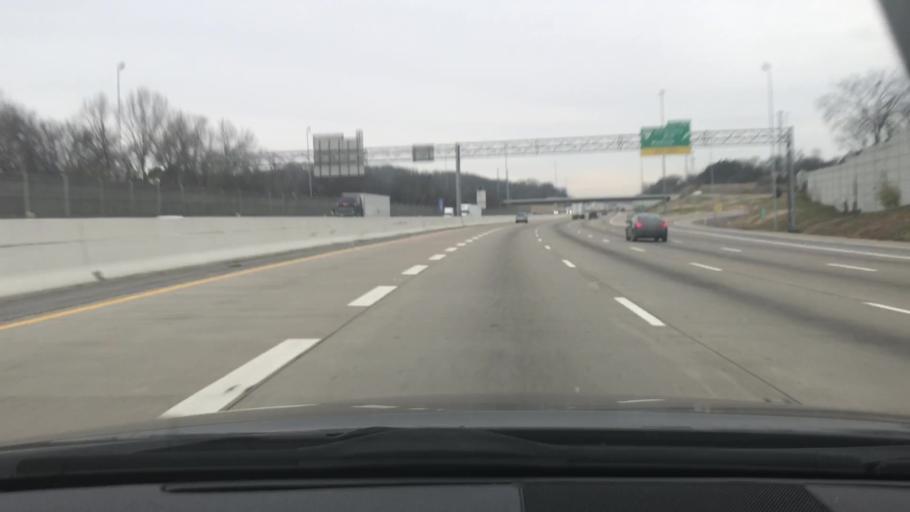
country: US
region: Tennessee
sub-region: Davidson County
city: Goodlettsville
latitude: 36.2602
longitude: -86.7383
